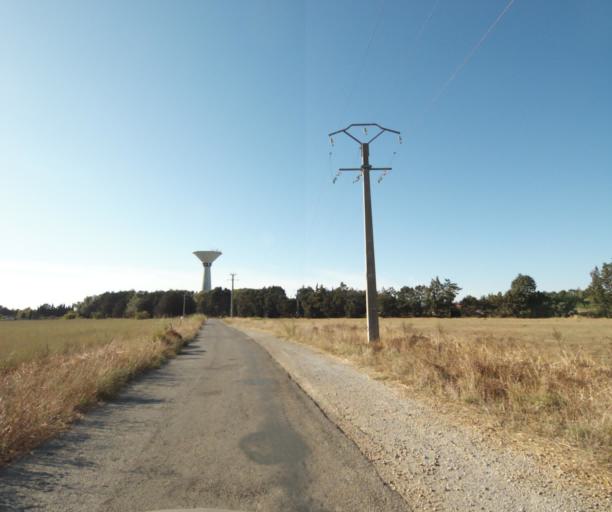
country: FR
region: Languedoc-Roussillon
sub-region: Departement du Gard
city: Garons
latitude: 43.7782
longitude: 4.4658
